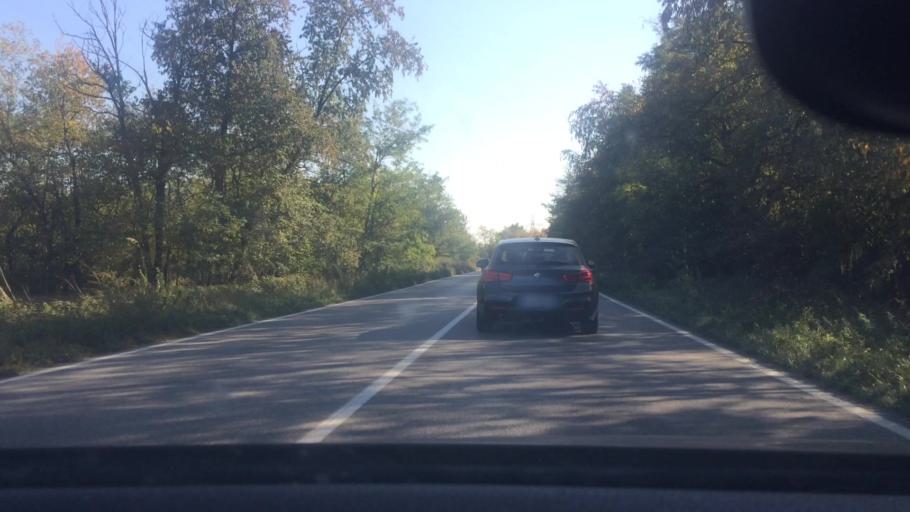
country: IT
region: Lombardy
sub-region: Citta metropolitana di Milano
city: Nerviano
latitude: 45.5336
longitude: 8.9678
